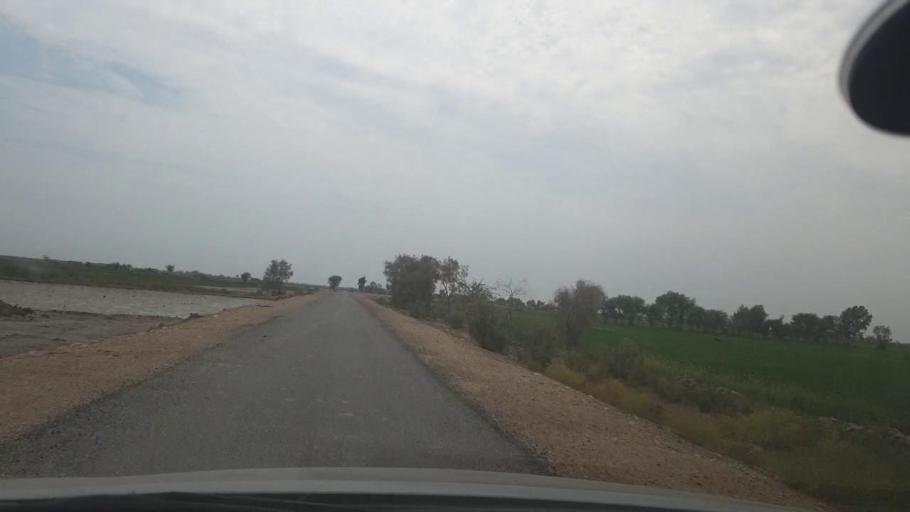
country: PK
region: Balochistan
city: Garhi Khairo
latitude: 28.0206
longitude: 68.0445
